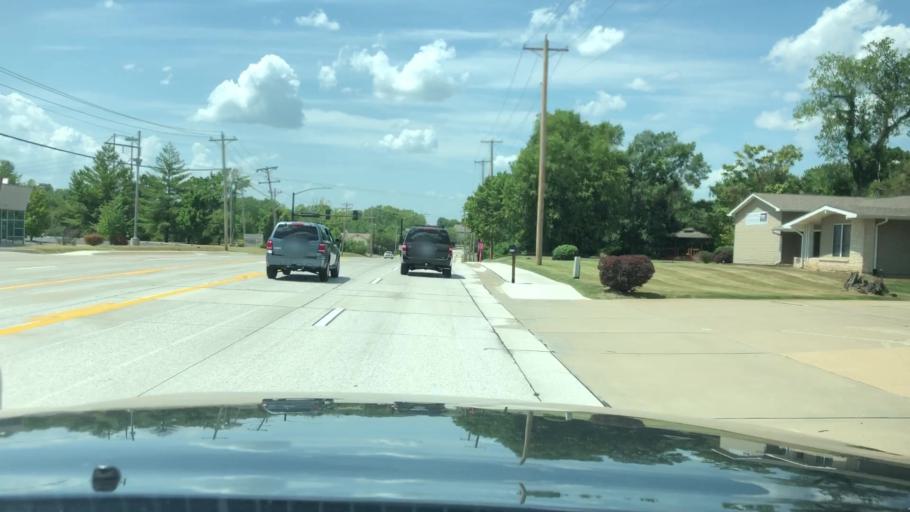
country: US
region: Missouri
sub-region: Saint Charles County
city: Saint Peters
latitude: 38.7892
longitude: -90.6394
